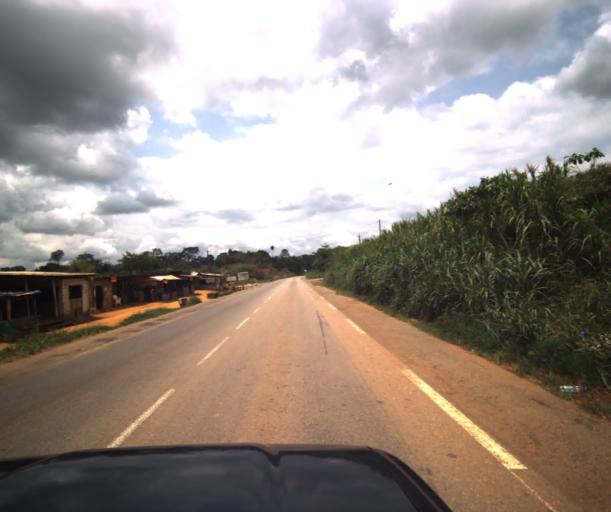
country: CM
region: Centre
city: Eseka
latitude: 3.8521
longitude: 10.9478
